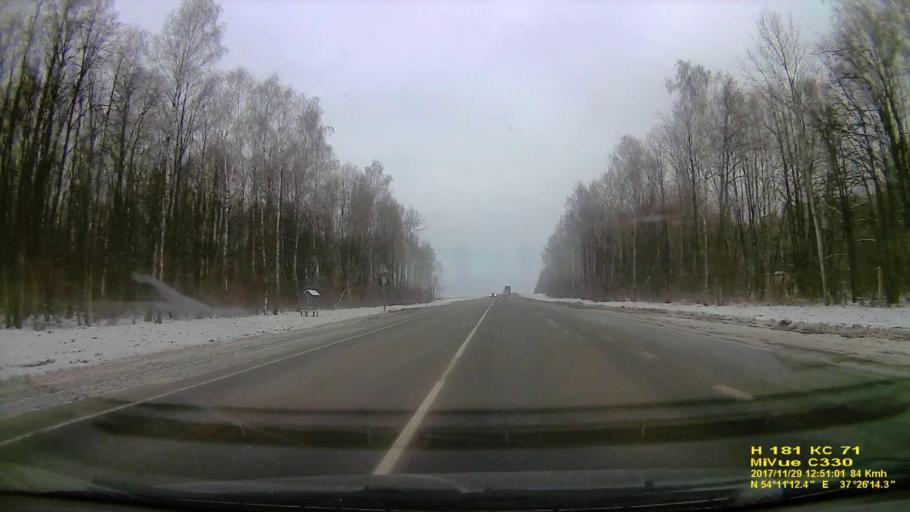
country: RU
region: Tula
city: Barsuki
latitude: 54.1868
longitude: 37.4373
